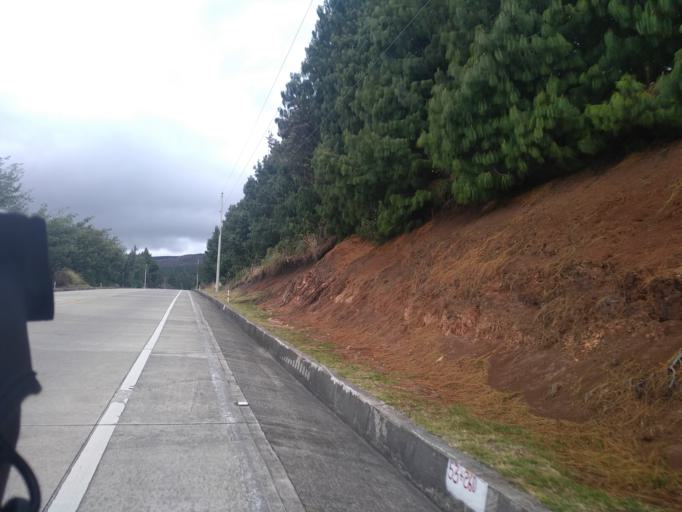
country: EC
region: Azuay
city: Cuenca
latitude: -3.3544
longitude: -79.1878
